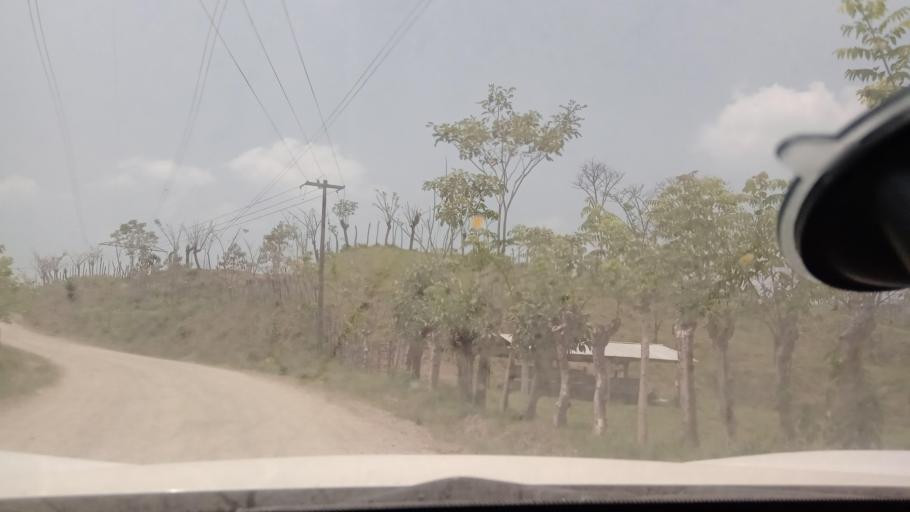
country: MX
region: Chiapas
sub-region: Tecpatan
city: Raudales Malpaso
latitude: 17.4462
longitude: -93.7891
